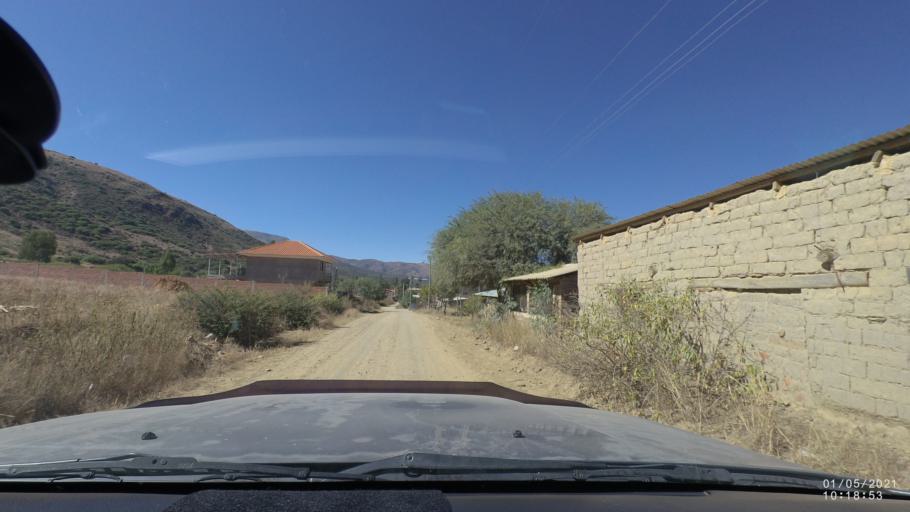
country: BO
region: Cochabamba
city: Capinota
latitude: -17.5566
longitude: -66.2075
